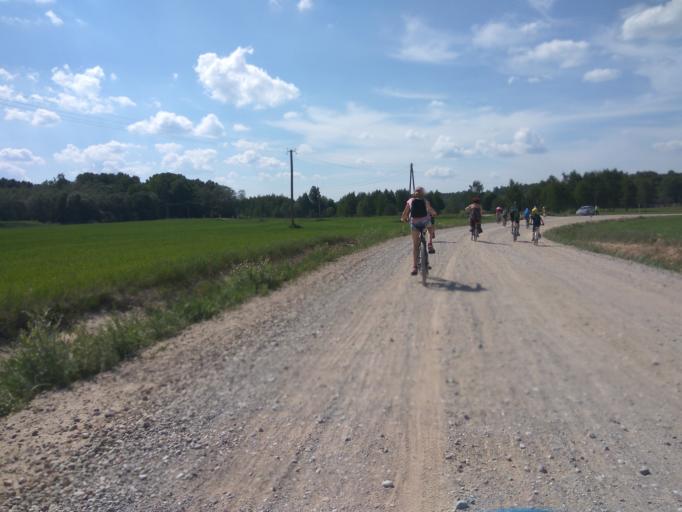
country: LV
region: Kuldigas Rajons
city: Kuldiga
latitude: 56.9403
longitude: 21.9728
